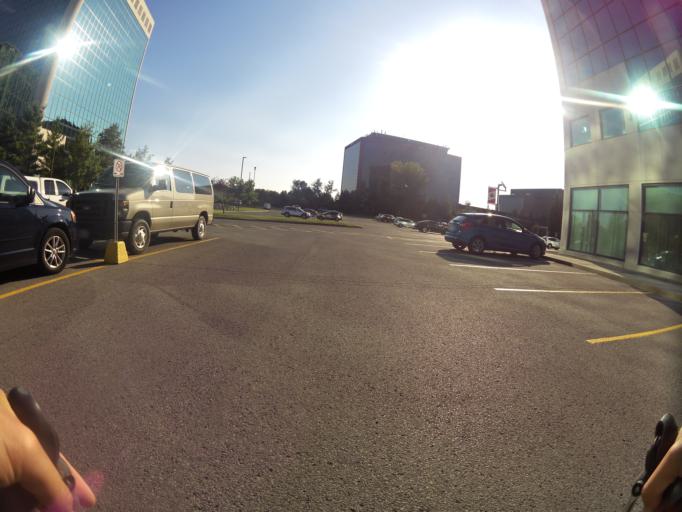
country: CA
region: Ontario
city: Bells Corners
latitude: 45.3486
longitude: -75.9189
